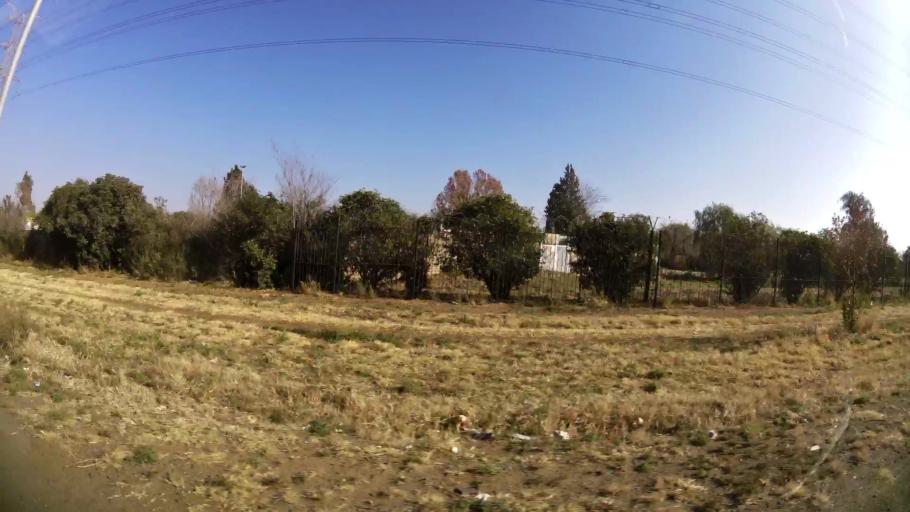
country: ZA
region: Orange Free State
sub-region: Mangaung Metropolitan Municipality
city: Bloemfontein
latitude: -29.1788
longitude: 26.1906
